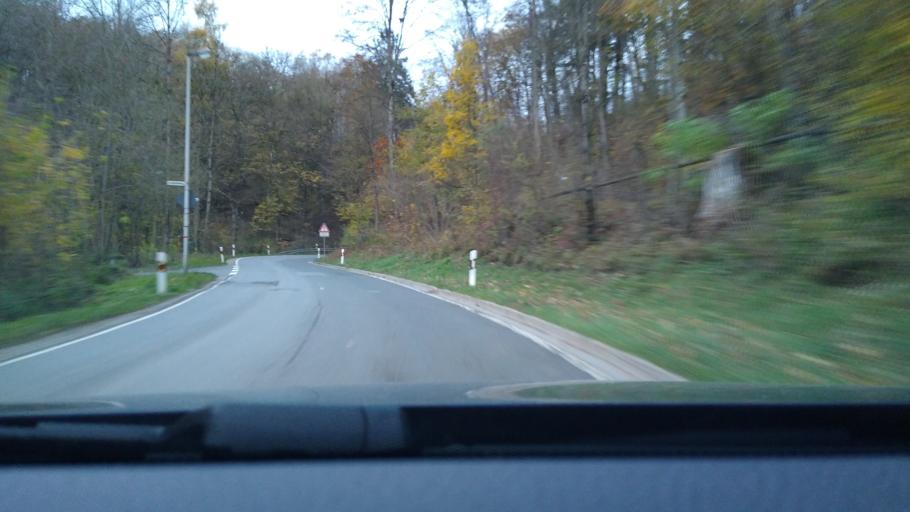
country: DE
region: Bavaria
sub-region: Upper Franconia
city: Grafenberg
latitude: 49.6509
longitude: 11.2496
